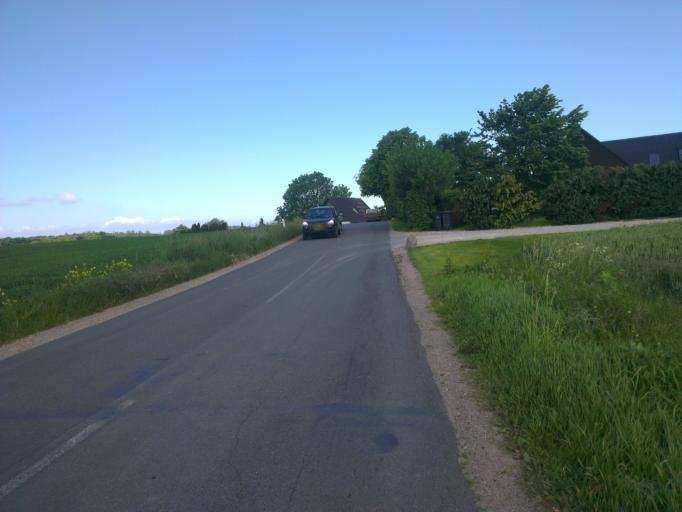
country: DK
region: Capital Region
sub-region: Frederikssund Kommune
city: Skibby
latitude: 55.7679
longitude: 11.9473
